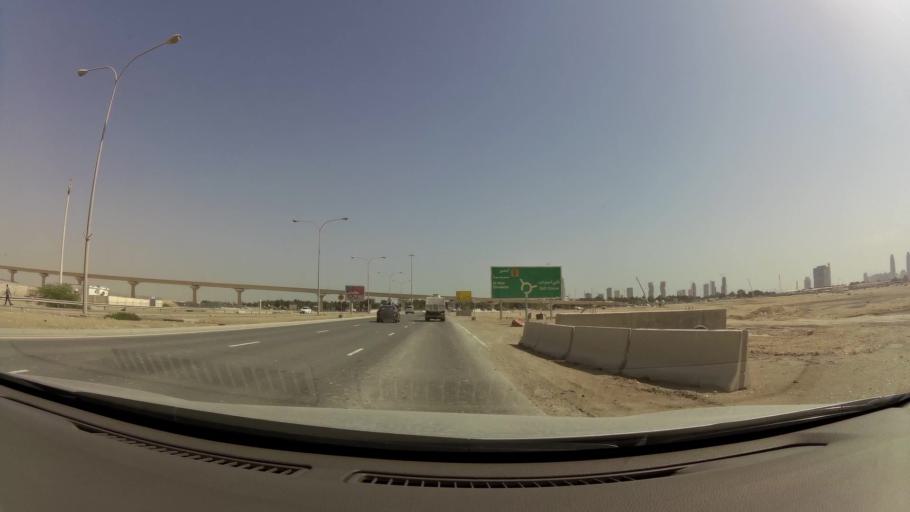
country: QA
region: Baladiyat ad Dawhah
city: Doha
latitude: 25.3758
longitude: 51.4989
